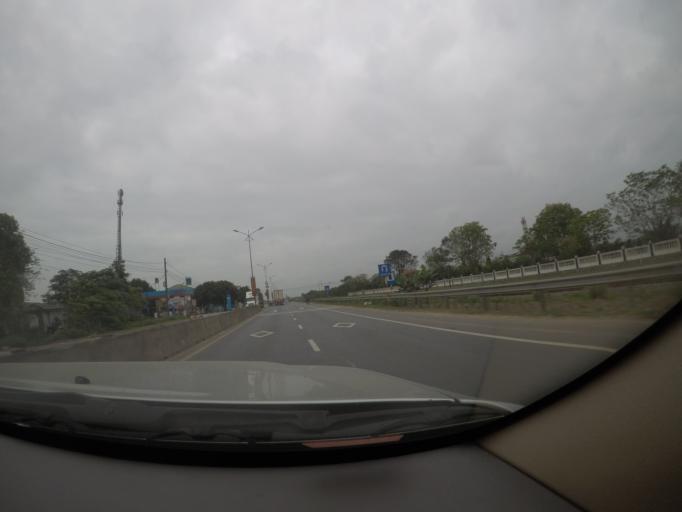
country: VN
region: Quang Tri
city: Hai Lang
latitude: 16.6850
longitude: 107.2508
